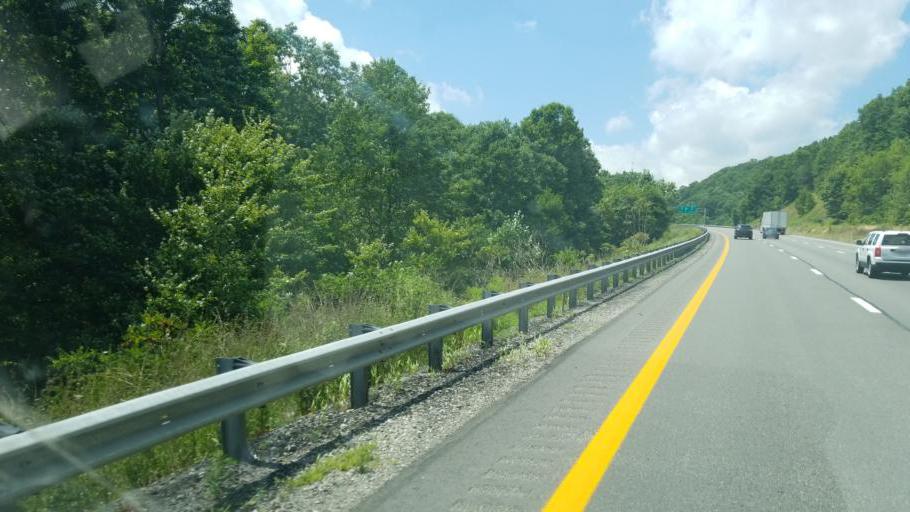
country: US
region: West Virginia
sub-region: Raleigh County
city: Beaver
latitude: 37.7208
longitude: -81.1702
